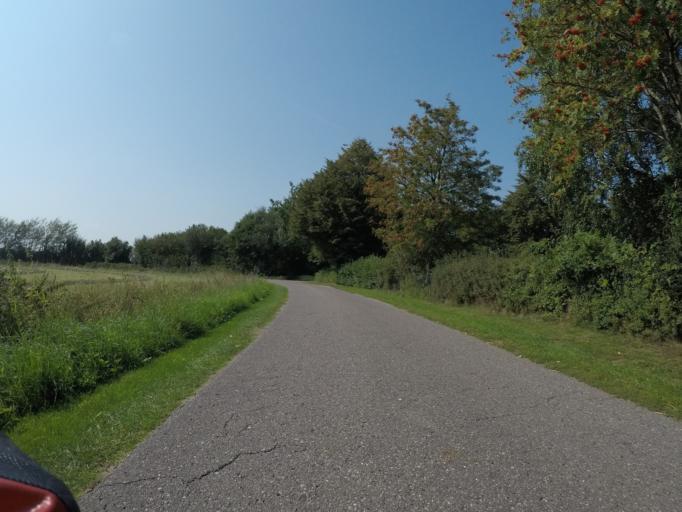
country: DE
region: Schleswig-Holstein
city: Stuvenborn
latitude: 53.8570
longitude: 10.1422
